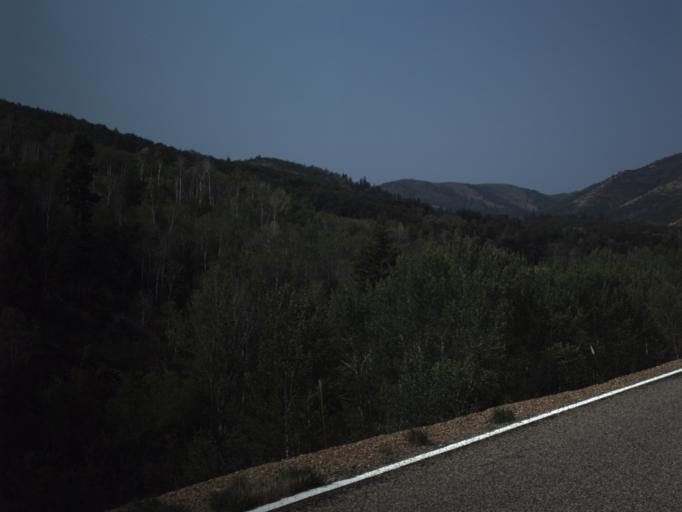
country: US
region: Utah
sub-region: Summit County
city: Summit Park
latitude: 40.8530
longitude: -111.6080
